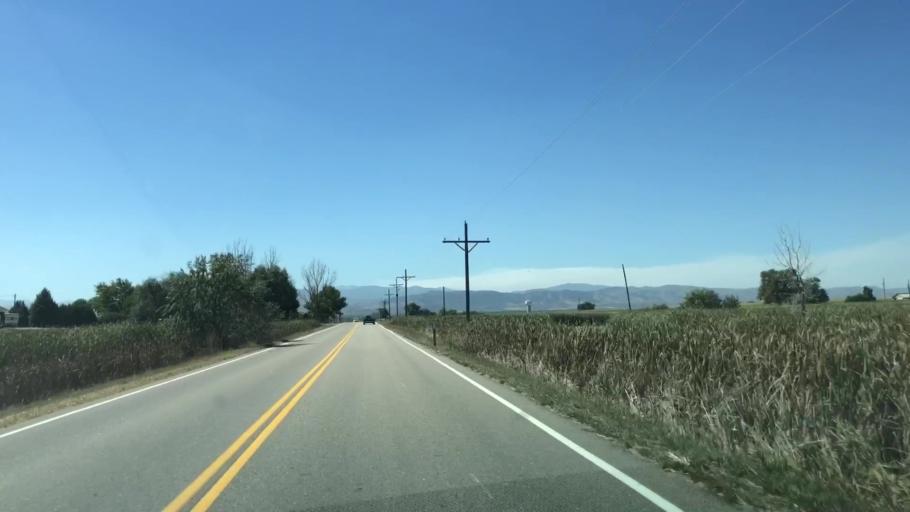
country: US
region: Colorado
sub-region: Weld County
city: Windsor
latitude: 40.5379
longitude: -104.9317
